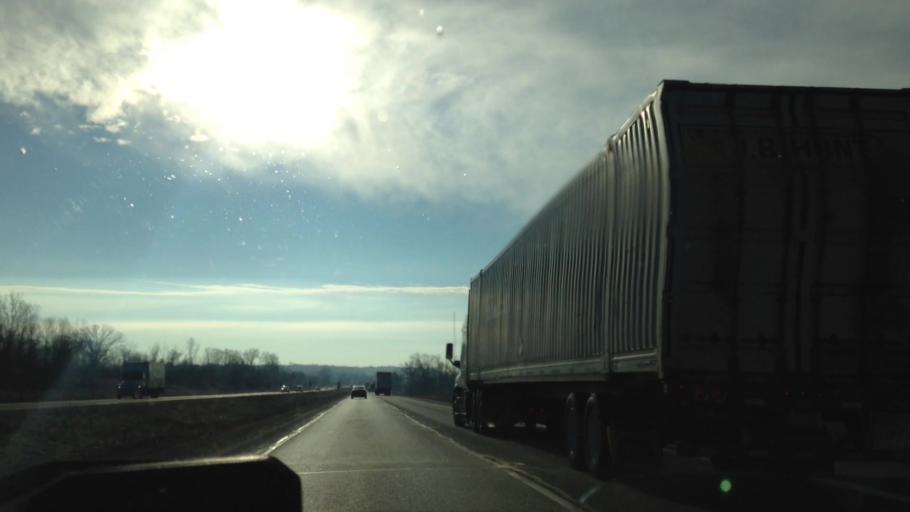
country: US
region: Wisconsin
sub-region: Washington County
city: Slinger
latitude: 43.3952
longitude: -88.3172
